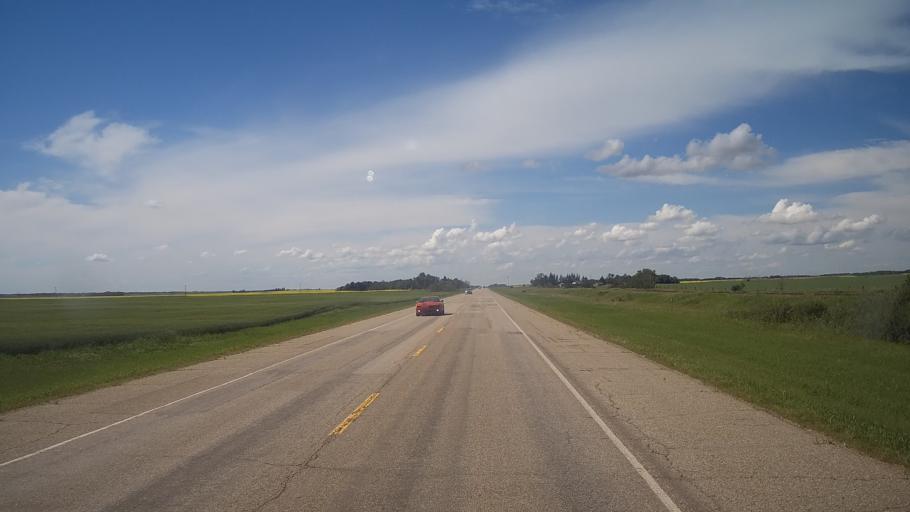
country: CA
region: Saskatchewan
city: Yorkton
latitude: 51.0862
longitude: -102.2544
